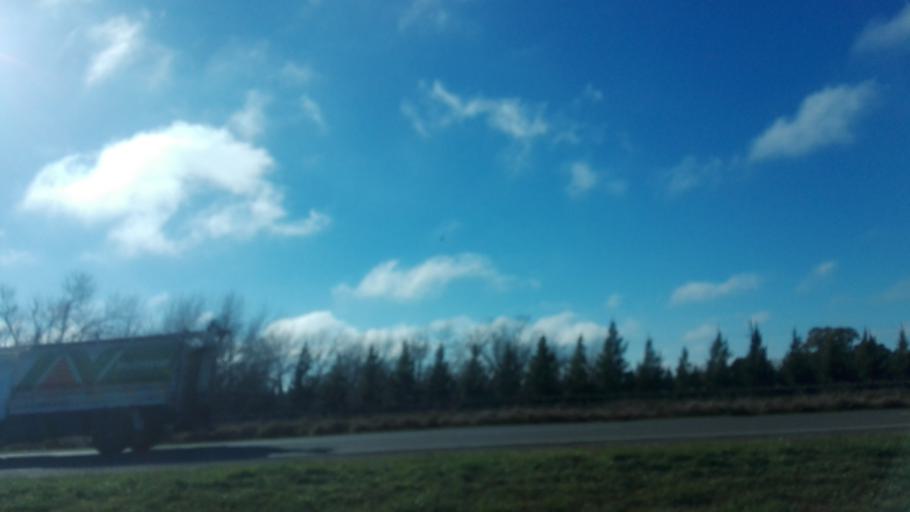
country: AR
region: Buenos Aires
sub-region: Partido de Castelli
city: Castelli
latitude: -35.8404
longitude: -57.9104
